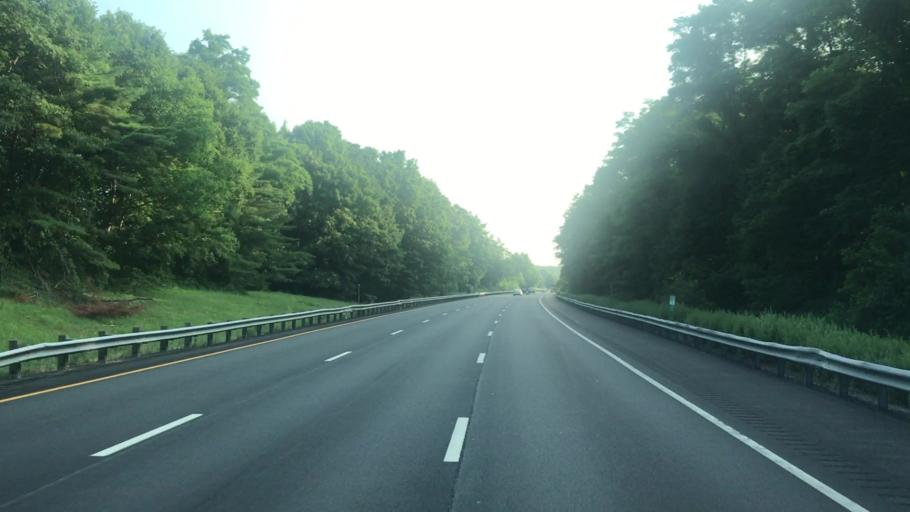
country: US
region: New York
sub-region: Westchester County
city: Bedford Hills
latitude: 41.2224
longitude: -73.6843
